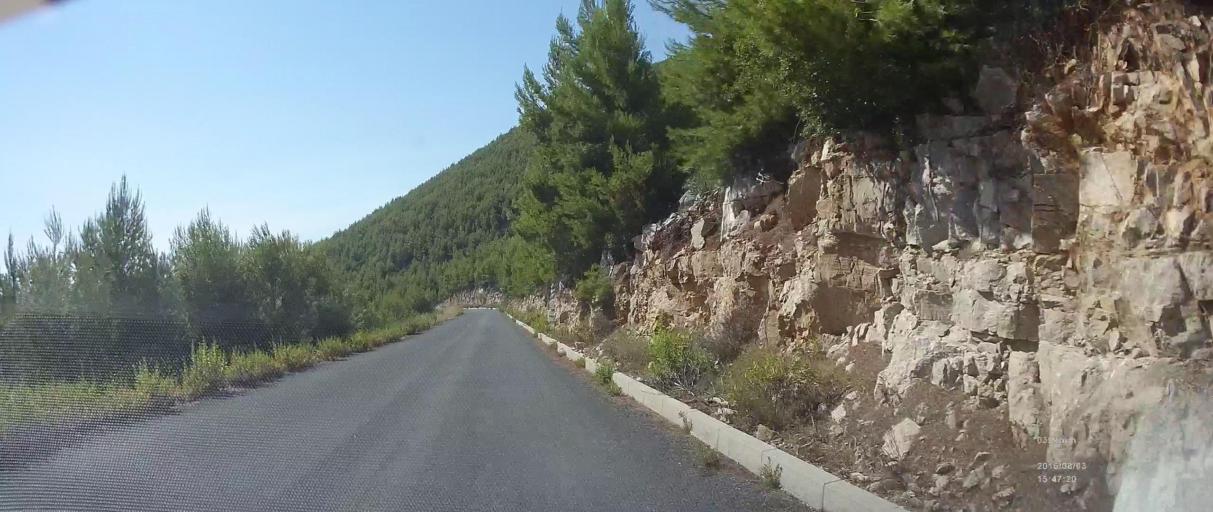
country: HR
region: Dubrovacko-Neretvanska
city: Blato
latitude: 42.7350
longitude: 17.5097
